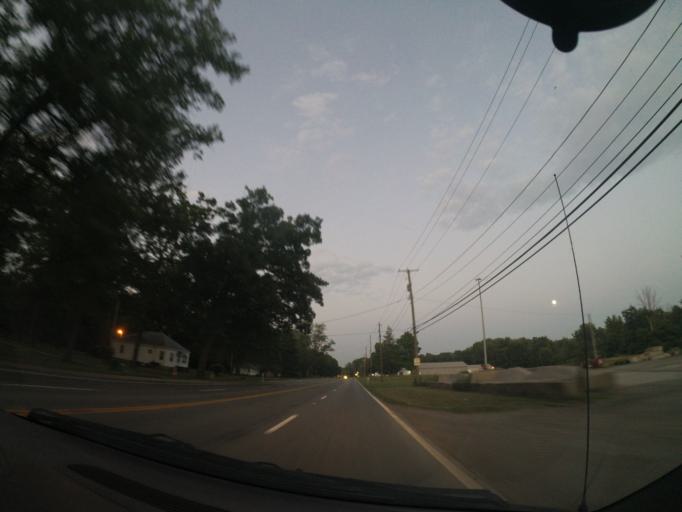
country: US
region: Ohio
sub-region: Lake County
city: North Madison
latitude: 41.7989
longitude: -81.0209
